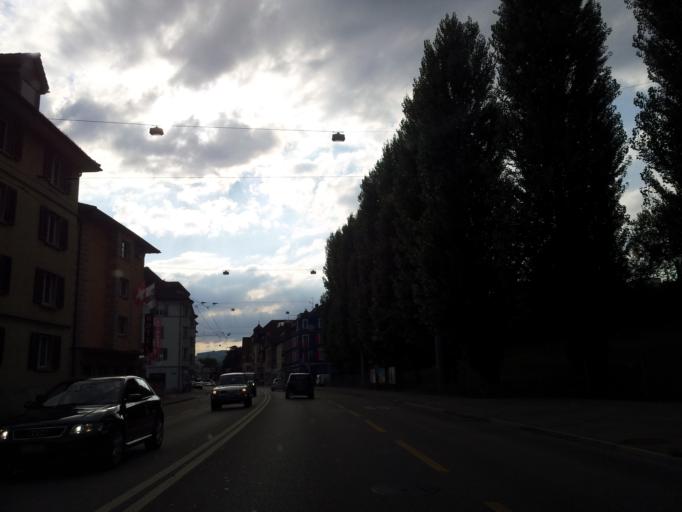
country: CH
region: Zurich
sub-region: Bezirk Dietikon
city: Schlieren / Boden
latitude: 47.3986
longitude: 8.4533
